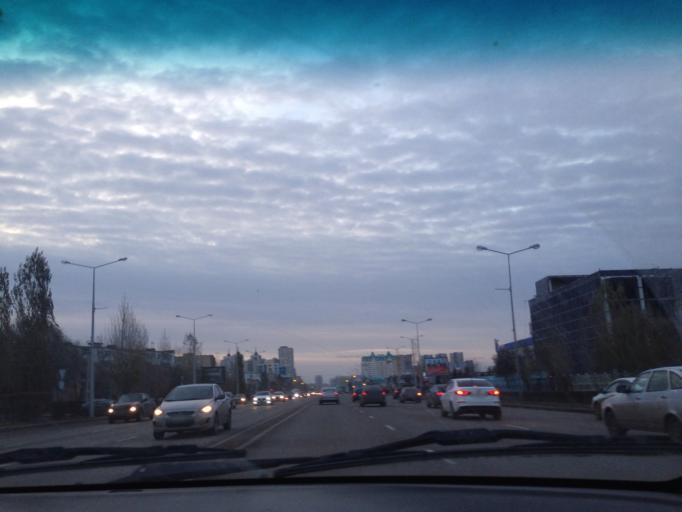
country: KZ
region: Astana Qalasy
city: Astana
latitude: 51.1481
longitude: 71.4585
